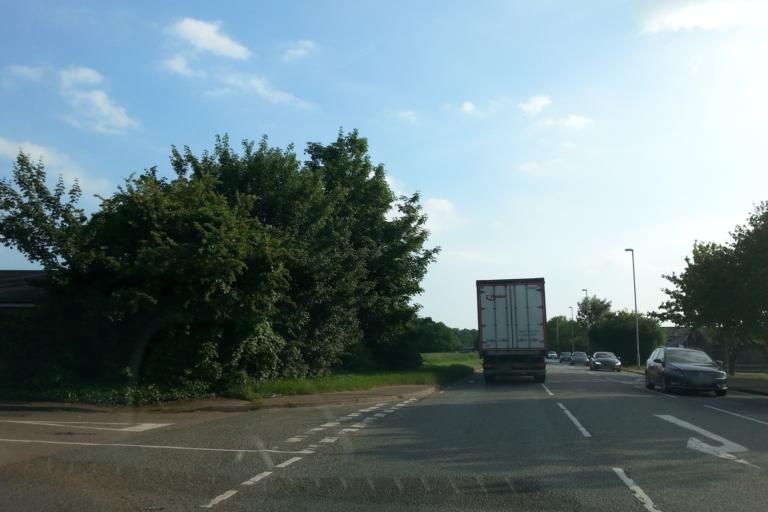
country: GB
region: England
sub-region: Cambridgeshire
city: Hemingford Grey
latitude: 52.3134
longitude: -0.0836
